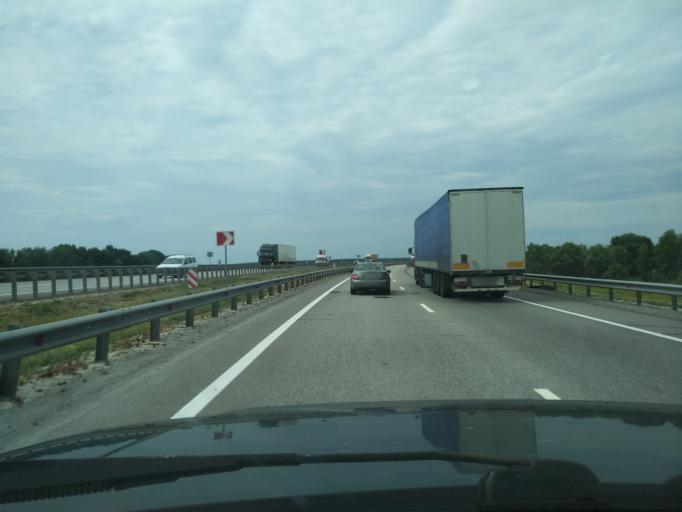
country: RU
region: Lipetsk
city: Khlevnoye
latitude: 52.0632
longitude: 39.1805
